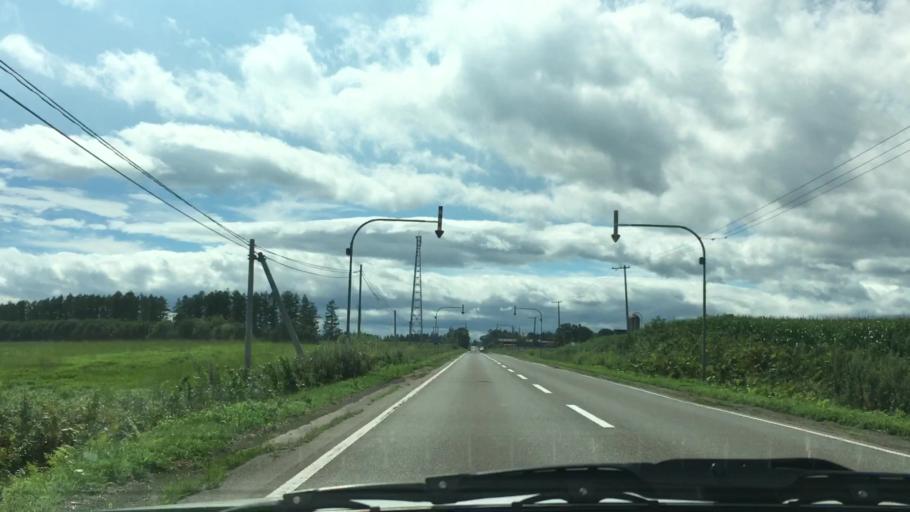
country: JP
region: Hokkaido
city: Otofuke
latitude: 43.2701
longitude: 143.3929
